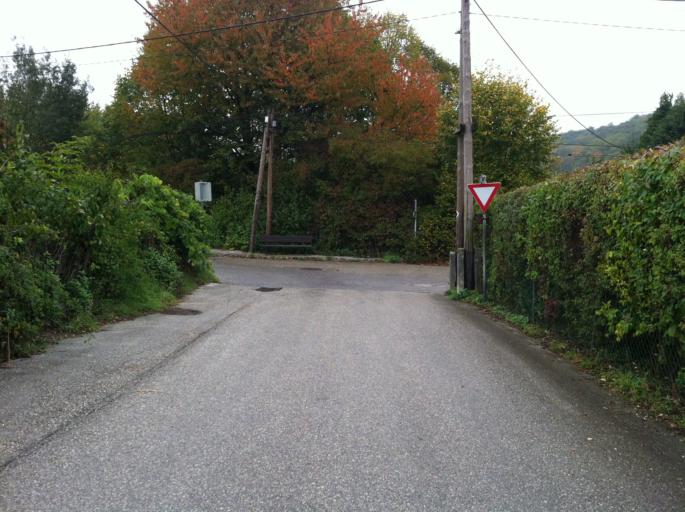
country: AT
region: Lower Austria
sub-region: Politischer Bezirk Wien-Umgebung
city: Gablitz
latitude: 48.2184
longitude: 16.1442
